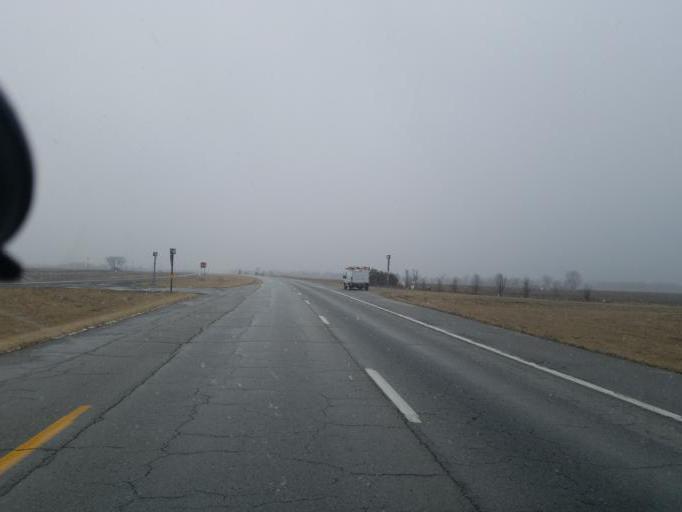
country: US
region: Missouri
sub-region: Macon County
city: La Plata
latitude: 39.9409
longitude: -92.4773
